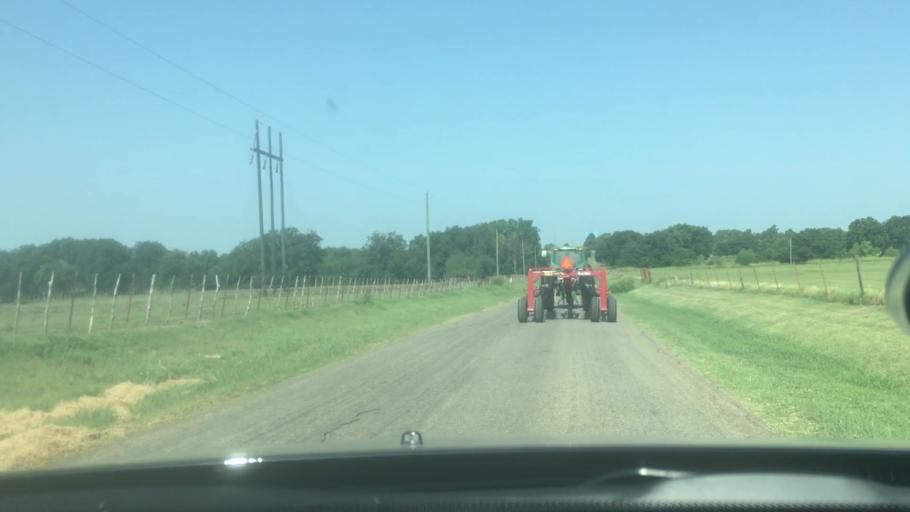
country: US
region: Oklahoma
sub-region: Bryan County
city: Calera
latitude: 33.9400
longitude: -96.4581
